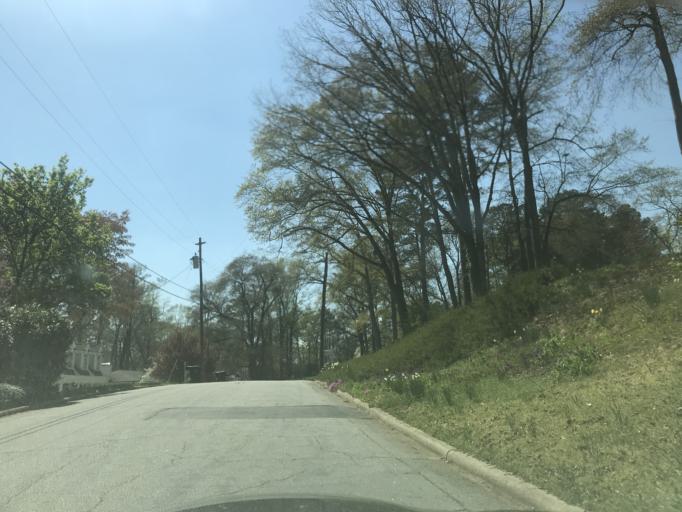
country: US
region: North Carolina
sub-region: Wake County
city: West Raleigh
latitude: 35.8248
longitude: -78.6384
